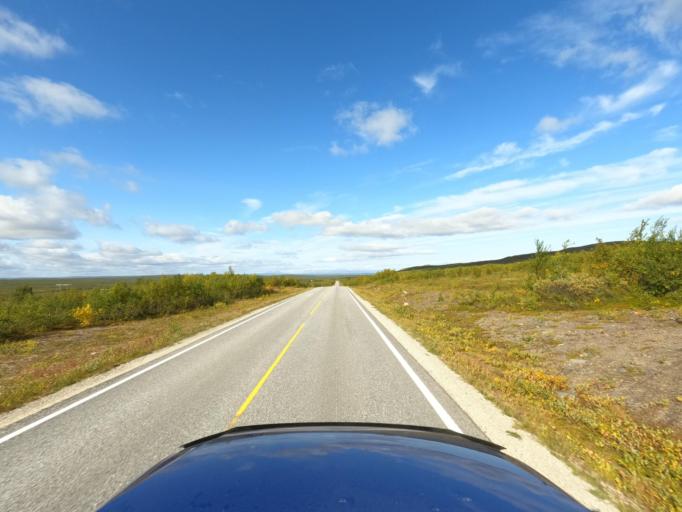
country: NO
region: Finnmark Fylke
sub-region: Karasjok
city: Karasjohka
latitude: 69.5580
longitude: 25.3961
